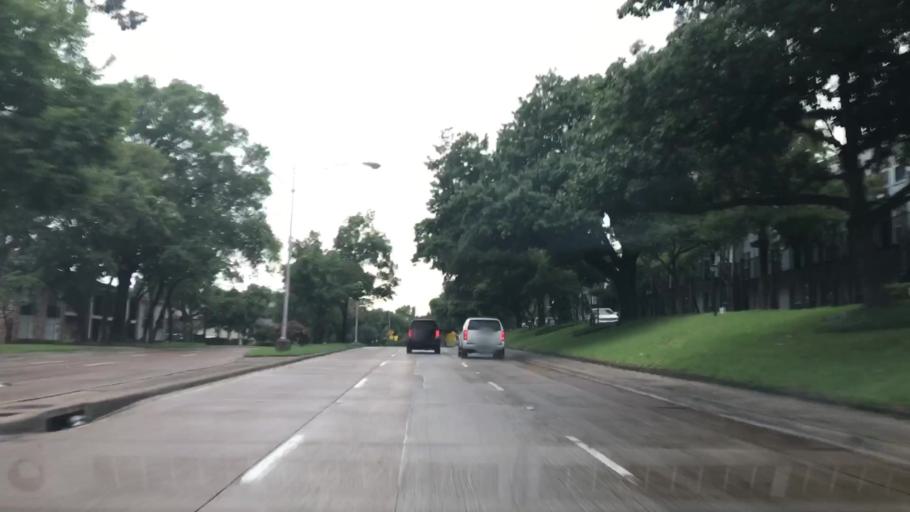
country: US
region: Texas
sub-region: Dallas County
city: University Park
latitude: 32.8985
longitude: -96.7714
